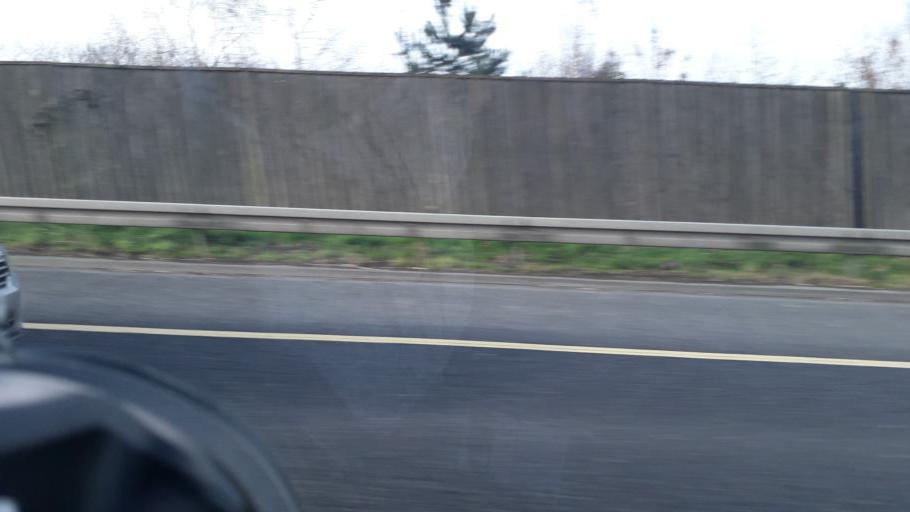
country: IE
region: Leinster
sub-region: Lu
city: Dundalk
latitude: 53.9892
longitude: -6.4366
